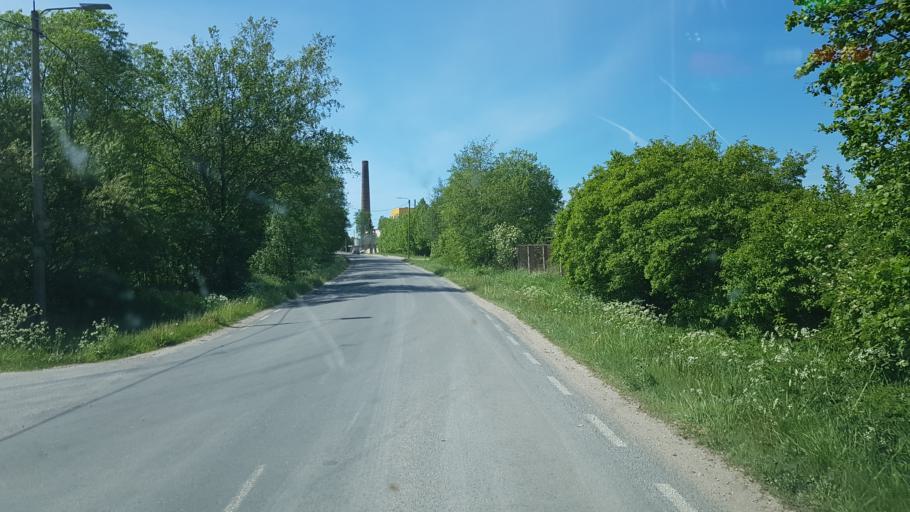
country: EE
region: Saare
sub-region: Kuressaare linn
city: Kuressaare
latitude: 58.2716
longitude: 22.4941
